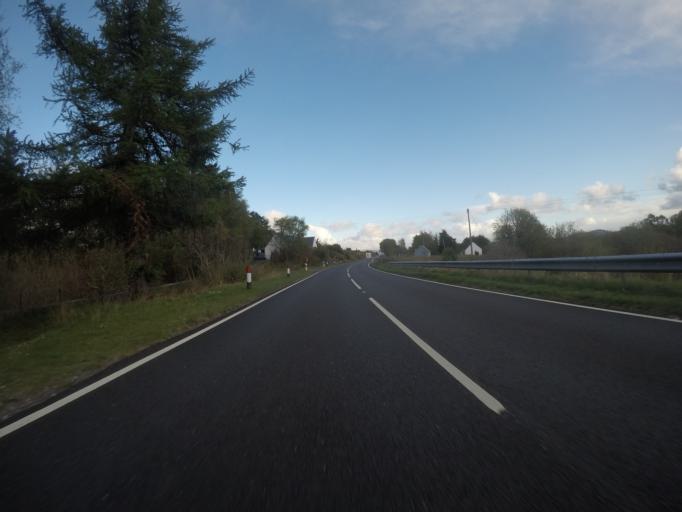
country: GB
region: Scotland
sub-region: Highland
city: Portree
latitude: 57.4985
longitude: -6.3237
